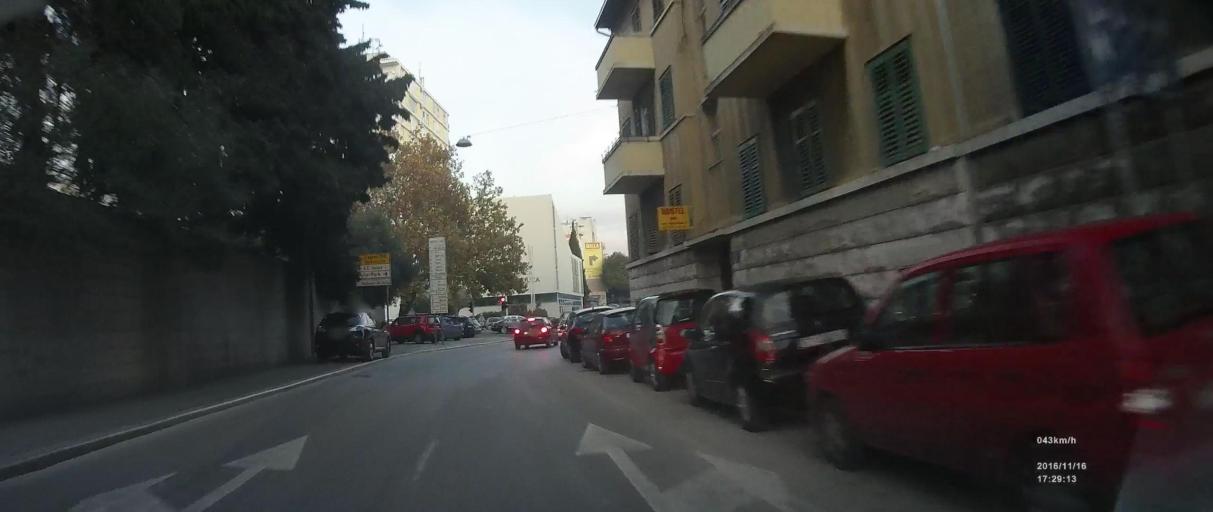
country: HR
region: Splitsko-Dalmatinska
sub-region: Grad Split
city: Split
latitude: 43.5055
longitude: 16.4469
